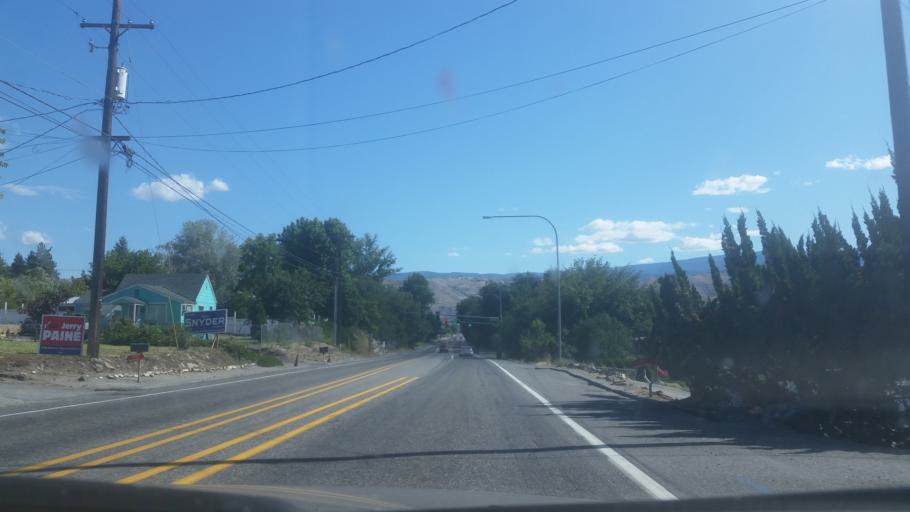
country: US
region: Washington
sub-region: Chelan County
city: Wenatchee
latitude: 47.4364
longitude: -120.2975
